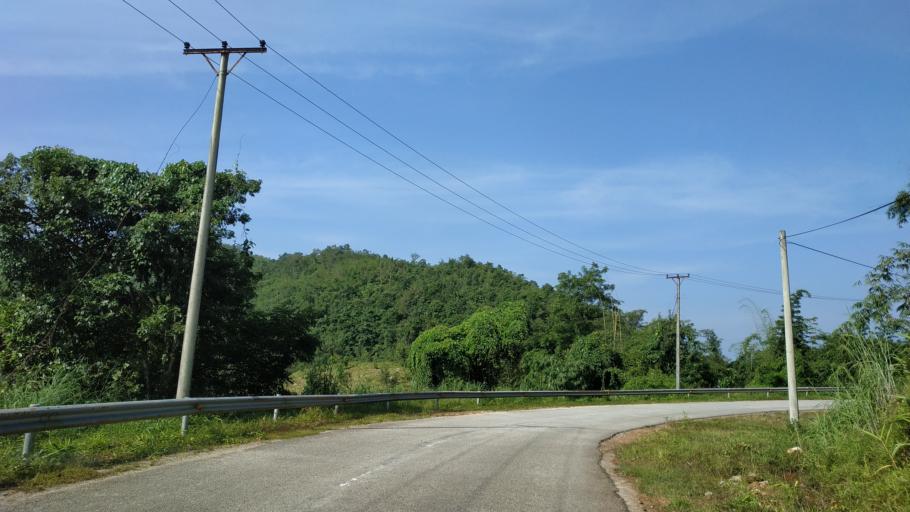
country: TH
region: Kanchanaburi
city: Thong Pha Phum
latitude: 14.6264
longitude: 98.1291
